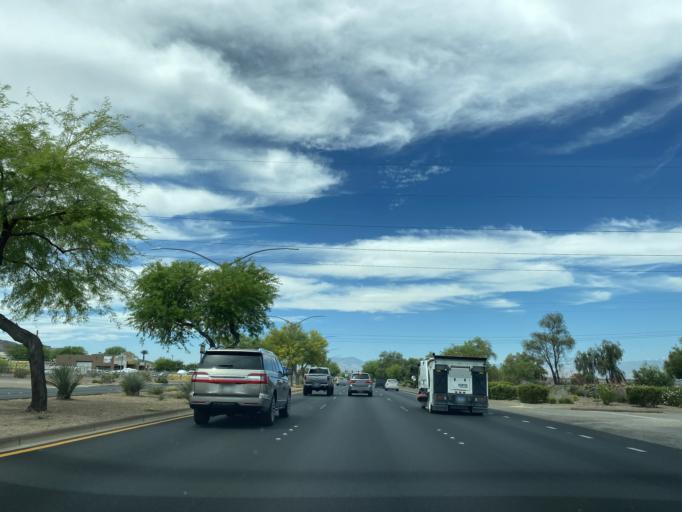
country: US
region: Nevada
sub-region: Clark County
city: Henderson
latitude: 36.0358
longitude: -114.9970
